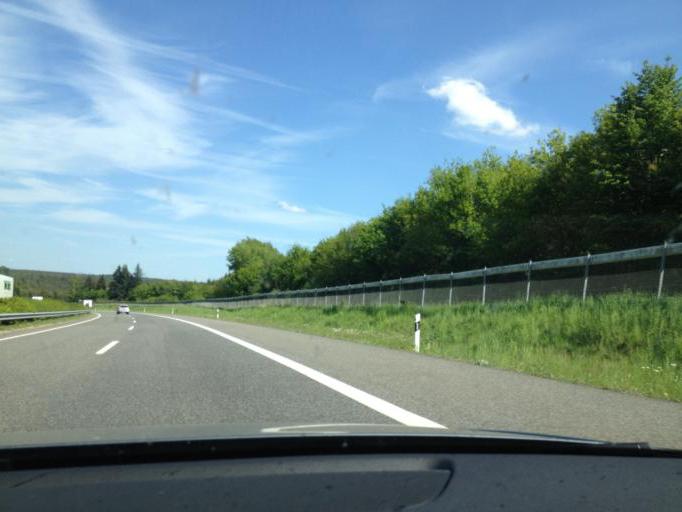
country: DE
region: Rheinland-Pfalz
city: Gransdorf
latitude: 50.0059
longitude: 6.7008
